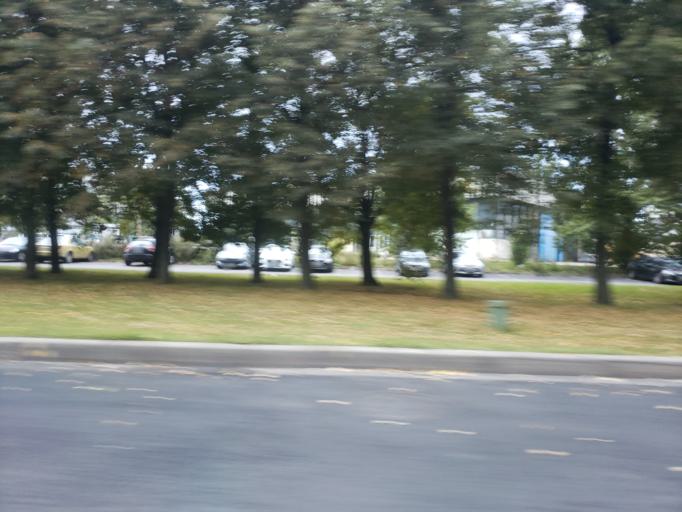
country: RU
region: St.-Petersburg
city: Vasyl'evsky Ostrov
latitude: 59.9277
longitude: 30.2378
